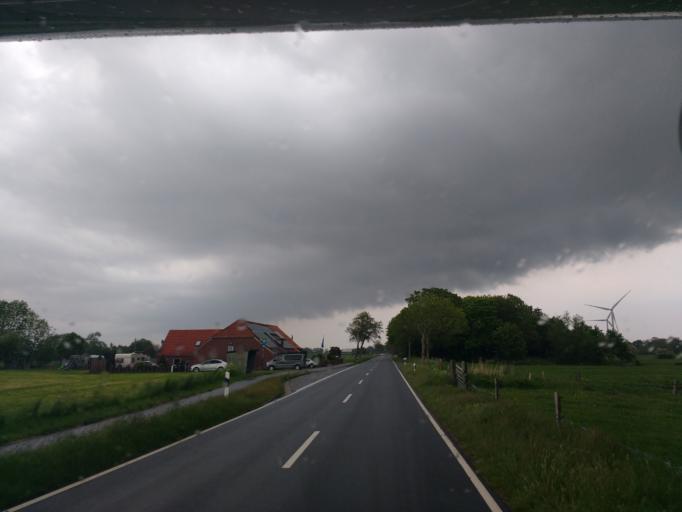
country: DE
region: Lower Saxony
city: Wangerooge
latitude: 53.6967
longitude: 7.9090
